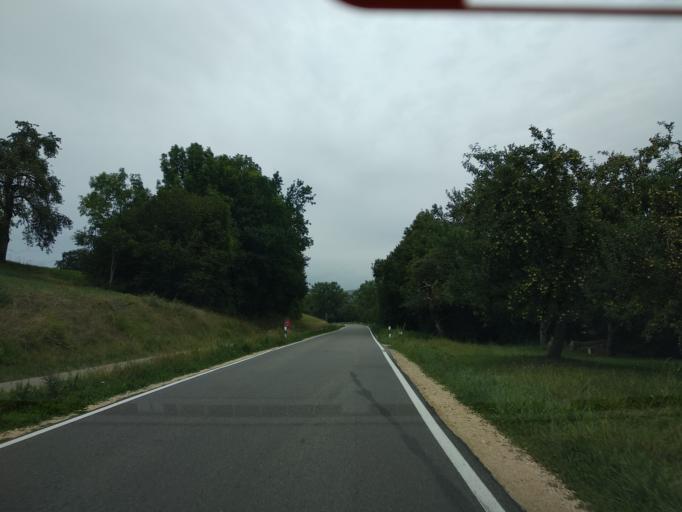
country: DE
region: Baden-Wuerttemberg
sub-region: Freiburg Region
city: Hilzingen
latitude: 47.7532
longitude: 8.7885
